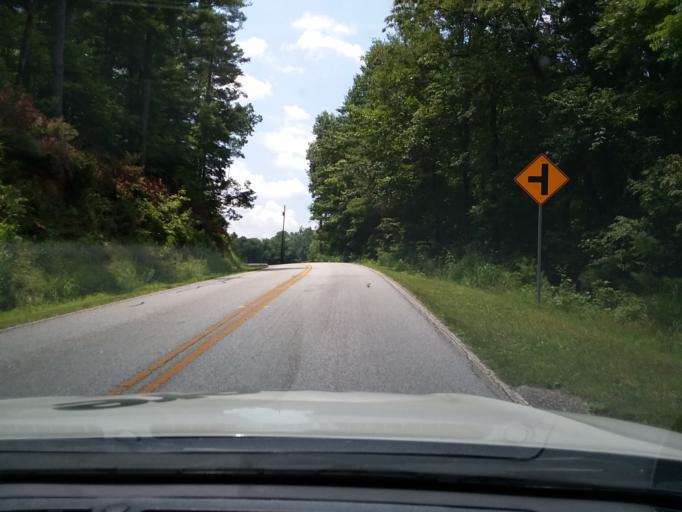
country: US
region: Georgia
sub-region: Rabun County
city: Mountain City
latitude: 34.9631
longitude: -83.1839
